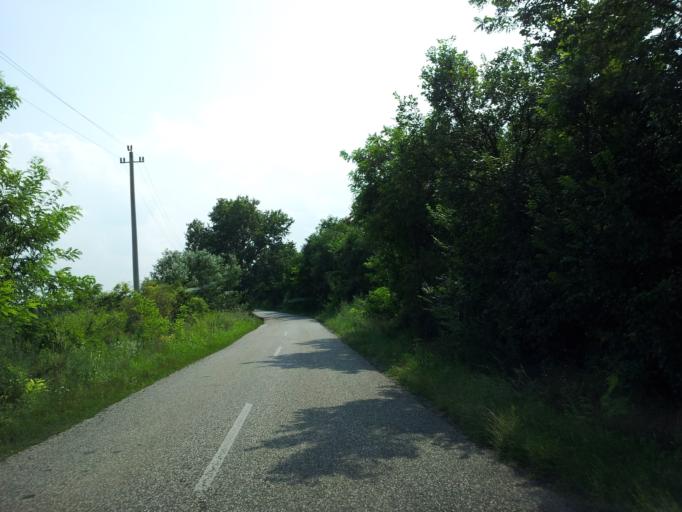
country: HU
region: Pest
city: Szigetujfalu
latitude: 47.2103
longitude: 18.9158
